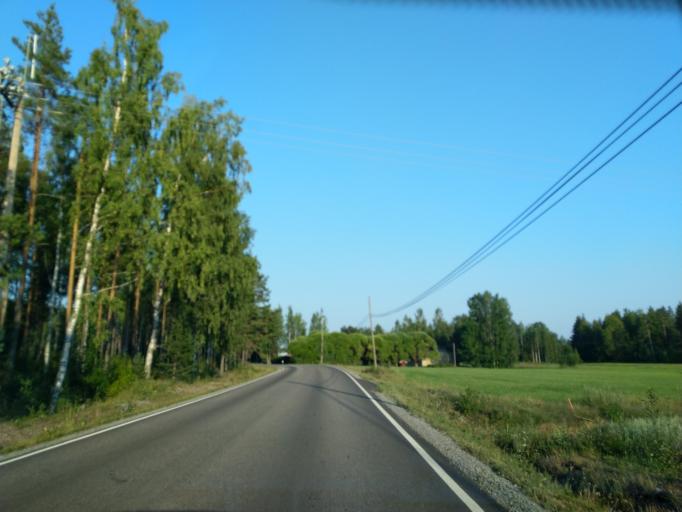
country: FI
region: Satakunta
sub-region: Pohjois-Satakunta
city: Honkajoki
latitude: 61.8210
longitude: 22.2170
